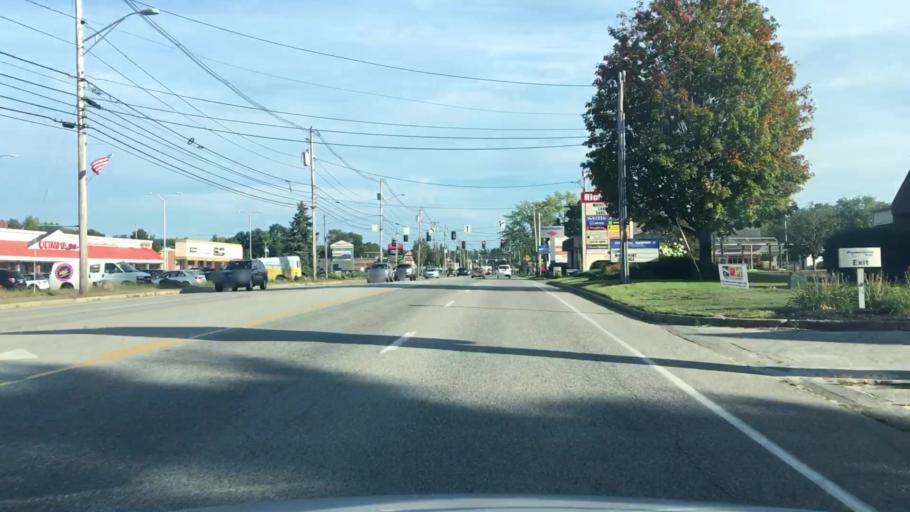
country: US
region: Maine
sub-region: Cumberland County
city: North Windham
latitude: 43.8375
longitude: -70.4413
